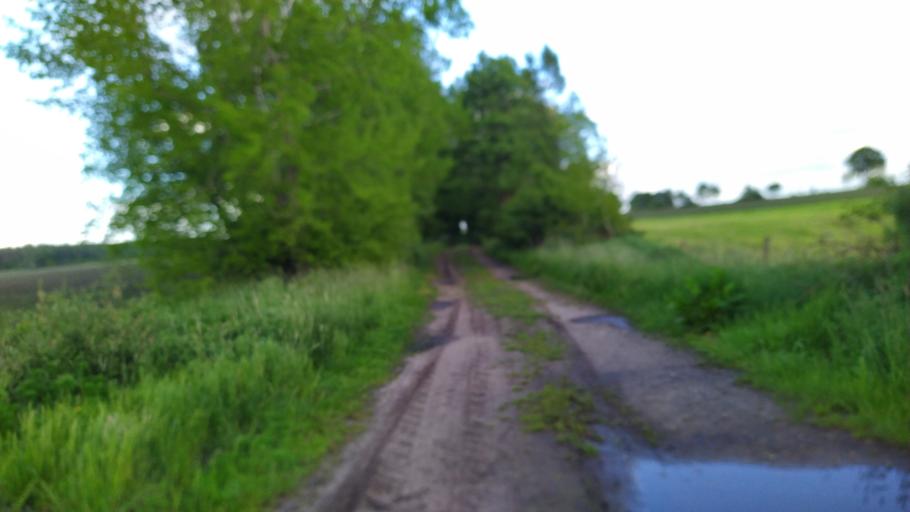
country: DE
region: Lower Saxony
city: Farven
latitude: 53.4543
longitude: 9.2940
